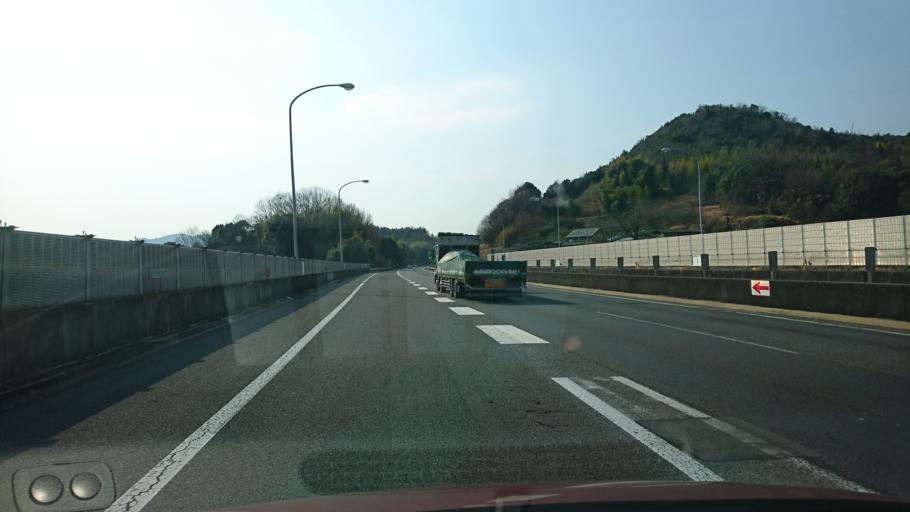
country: JP
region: Hiroshima
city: Fukuyama
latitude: 34.4882
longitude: 133.3141
